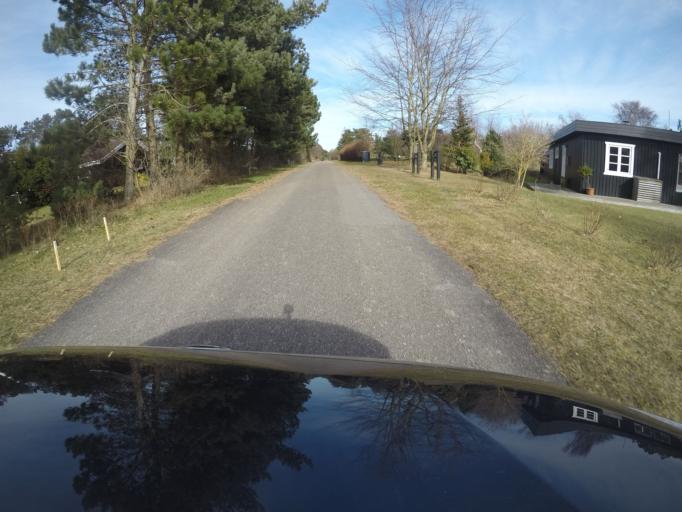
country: DK
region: Capital Region
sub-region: Halsnaes Kommune
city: Liseleje
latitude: 55.9946
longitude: 11.9153
